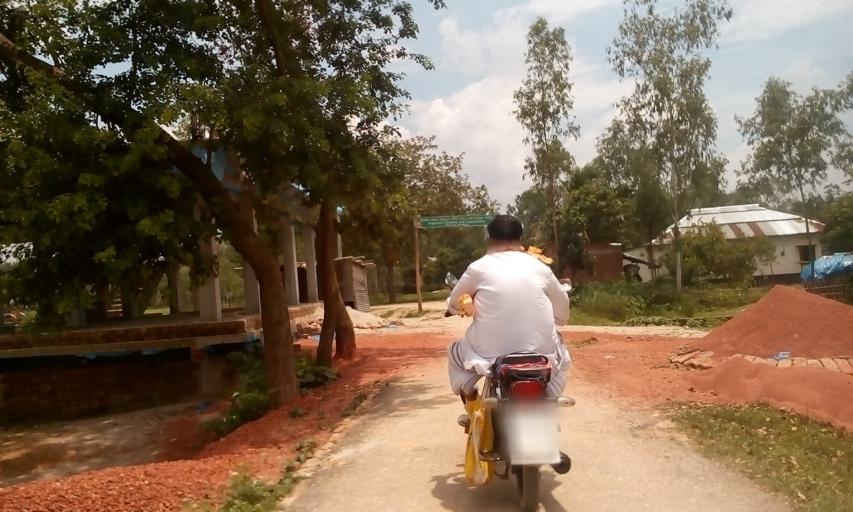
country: BD
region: Rangpur Division
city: Parbatipur
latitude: 25.4002
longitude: 88.9881
